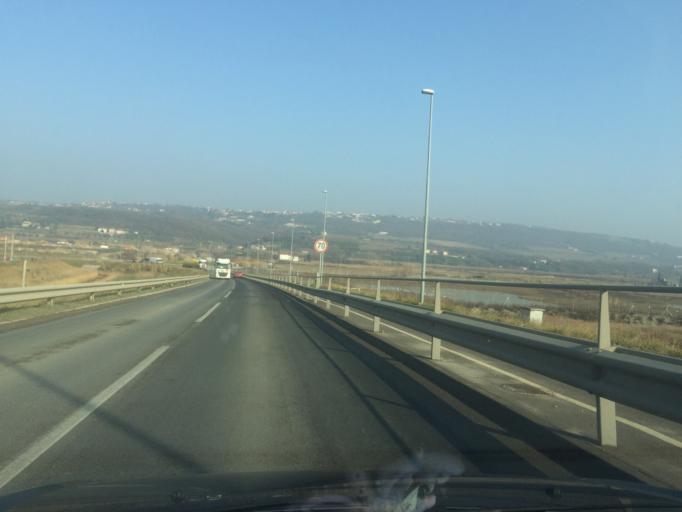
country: SI
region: Koper-Capodistria
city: Hrvatini
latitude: 45.5598
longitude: 13.7575
